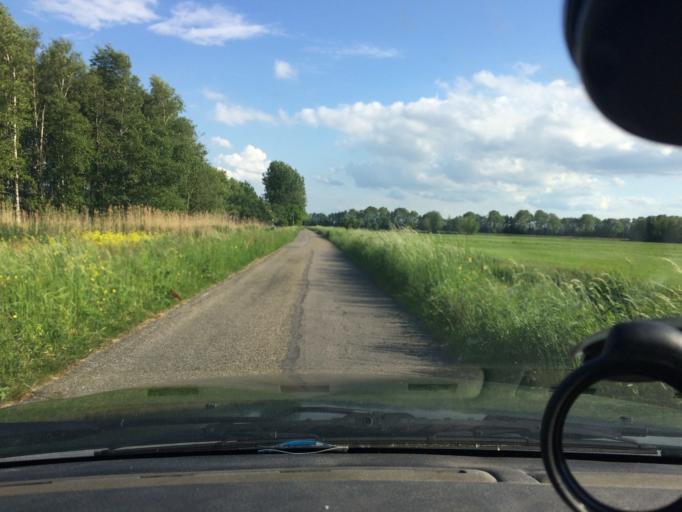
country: NL
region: North Holland
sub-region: Gemeente Haarlem
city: Haarlem
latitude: 52.3907
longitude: 4.7128
